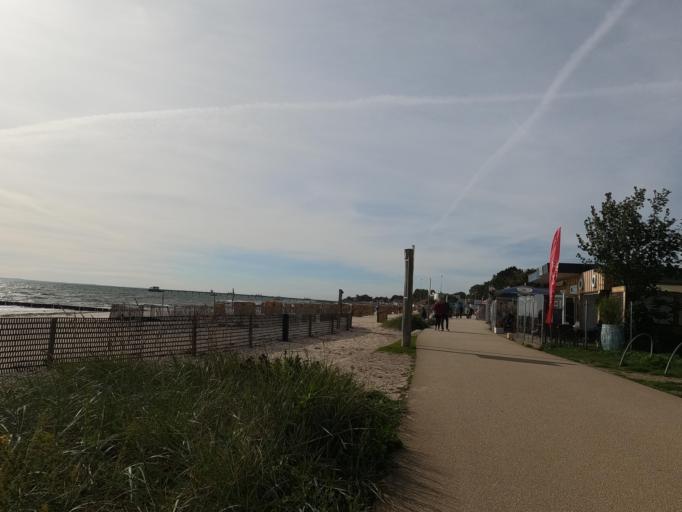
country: DE
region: Schleswig-Holstein
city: Kellenhusen
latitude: 54.1923
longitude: 11.0678
